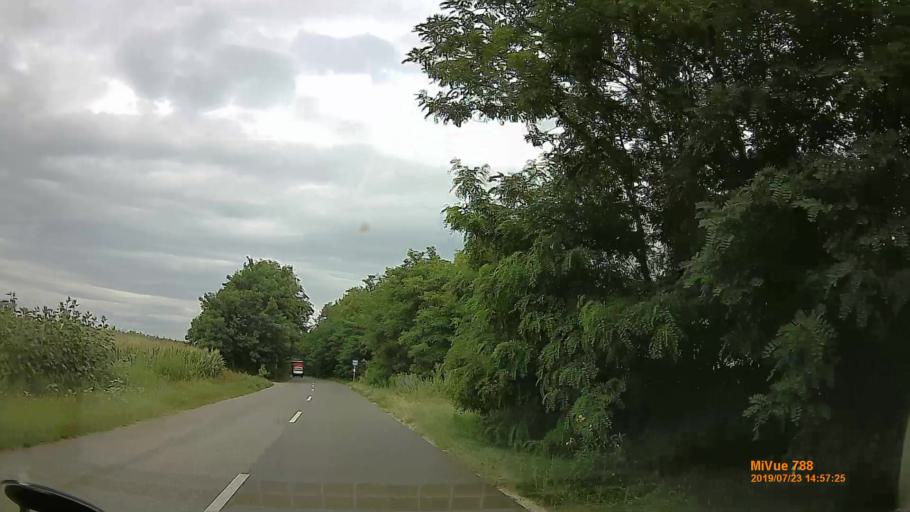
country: HU
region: Szabolcs-Szatmar-Bereg
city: Nyiregyhaza
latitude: 47.9057
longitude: 21.6714
